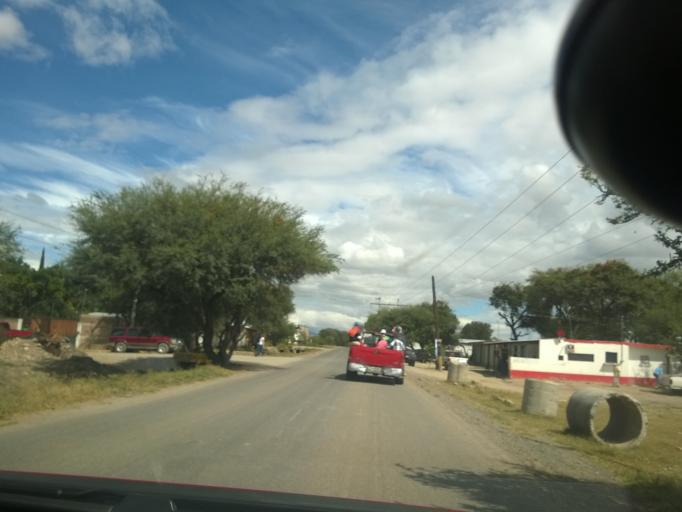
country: MX
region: Guanajuato
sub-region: Leon
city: Plan Guanajuato (La Sandia)
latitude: 20.9616
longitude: -101.6450
